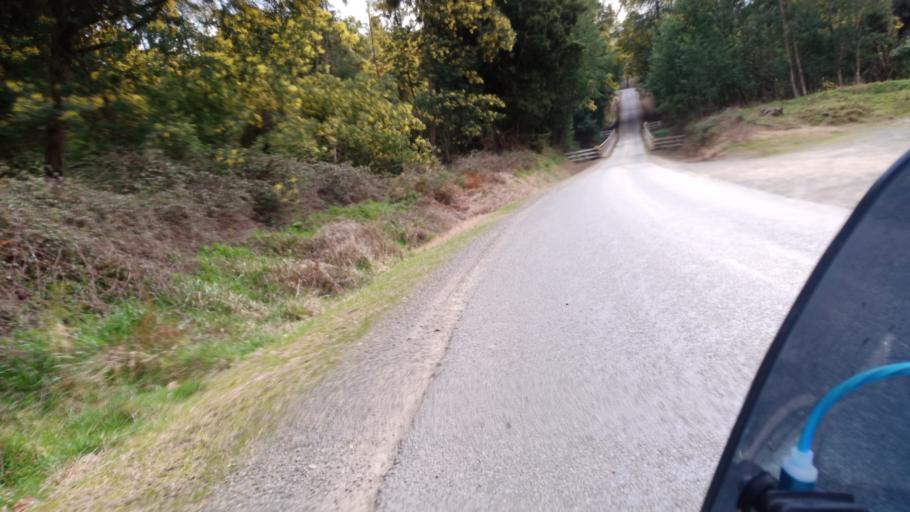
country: NZ
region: Hawke's Bay
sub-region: Wairoa District
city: Wairoa
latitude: -38.7733
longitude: 177.4162
